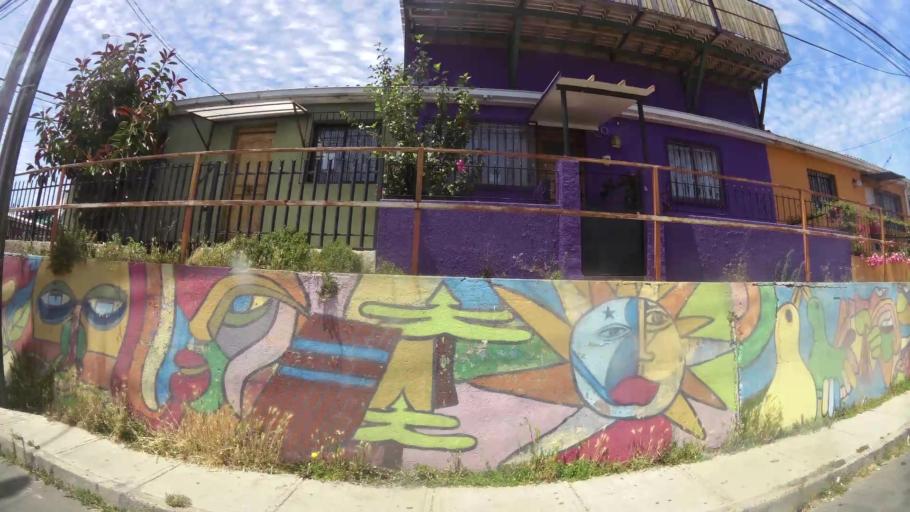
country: CL
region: Valparaiso
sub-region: Provincia de Valparaiso
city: Valparaiso
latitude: -33.0480
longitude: -71.5941
